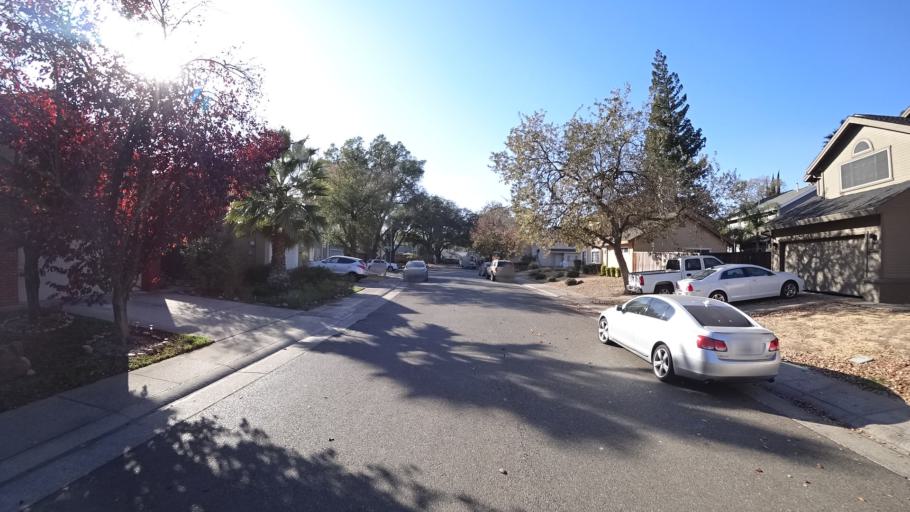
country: US
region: California
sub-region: Sacramento County
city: Antelope
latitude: 38.6960
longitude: -121.3110
